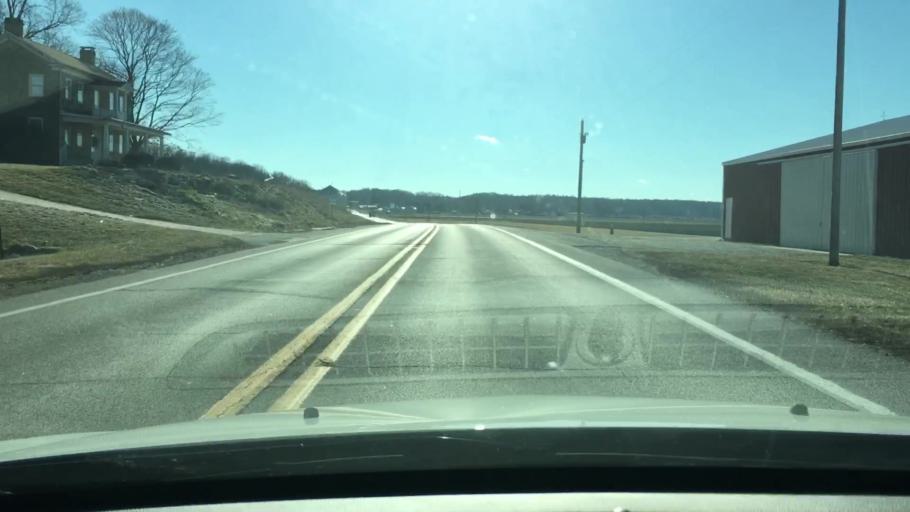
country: US
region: Illinois
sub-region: Morgan County
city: Meredosia
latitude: 39.7662
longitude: -90.5337
